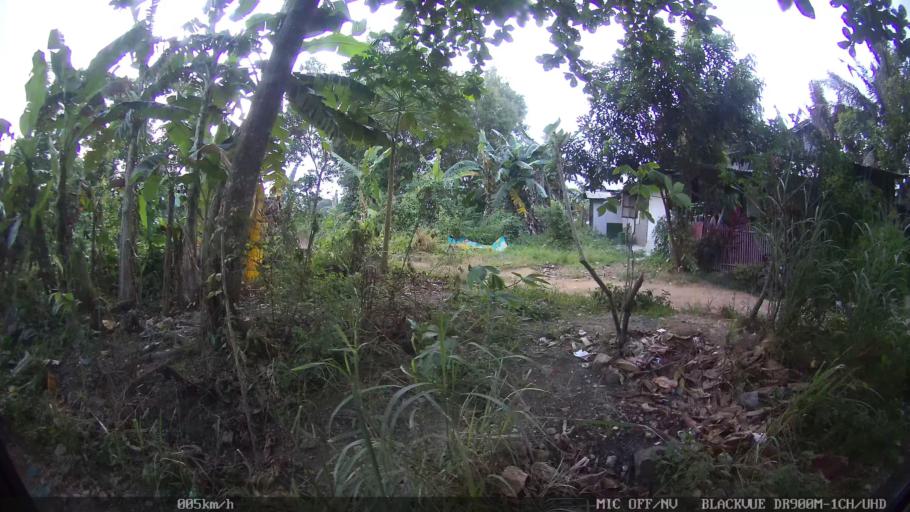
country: ID
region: Lampung
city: Kedaton
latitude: -5.4020
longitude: 105.2966
